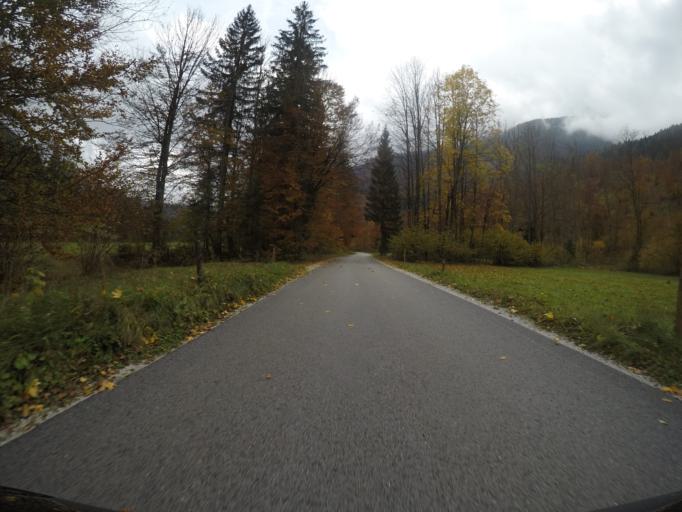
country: SI
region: Jesenice
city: Hrusica
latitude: 46.4241
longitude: 13.9731
